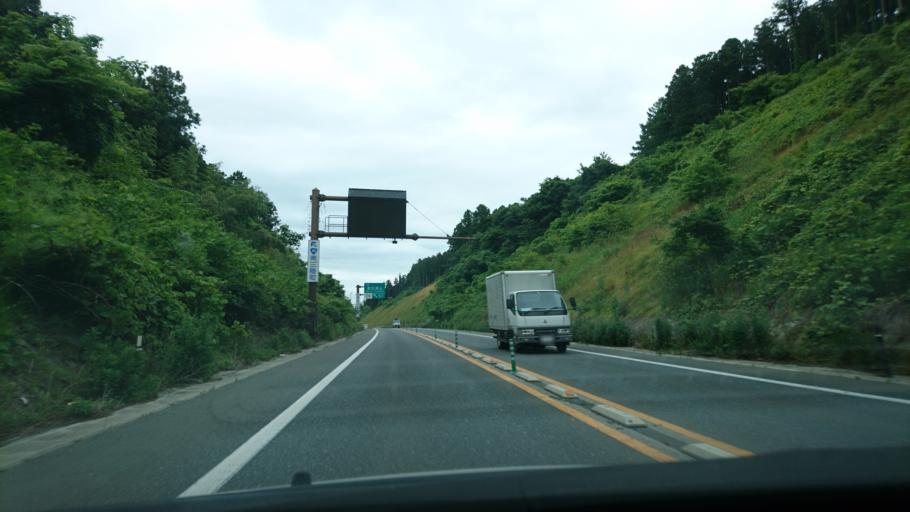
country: JP
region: Miyagi
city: Wakuya
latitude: 38.5920
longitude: 141.2800
